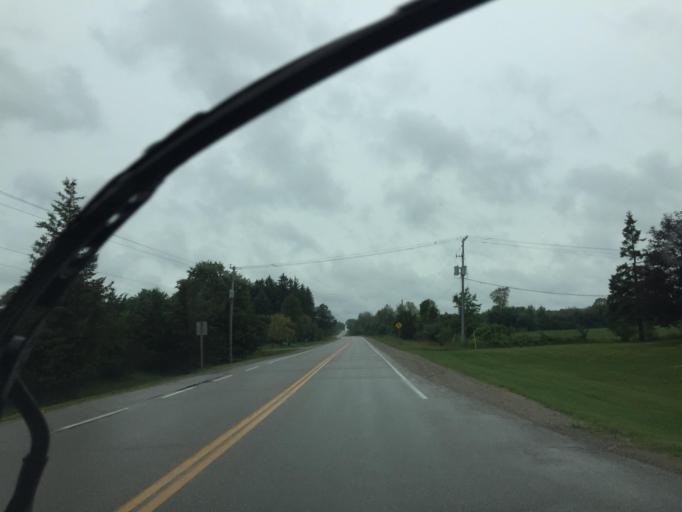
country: CA
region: Ontario
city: Cambridge
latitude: 43.4314
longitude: -80.2607
